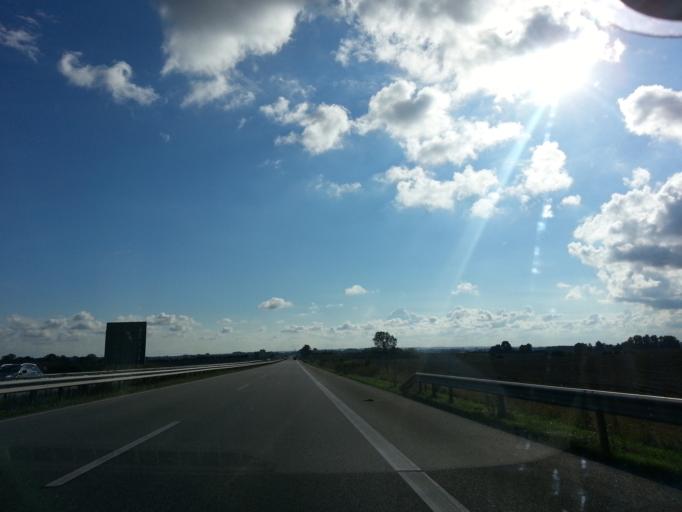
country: DE
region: Schleswig-Holstein
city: Heiligenhafen
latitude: 54.3549
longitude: 10.9564
